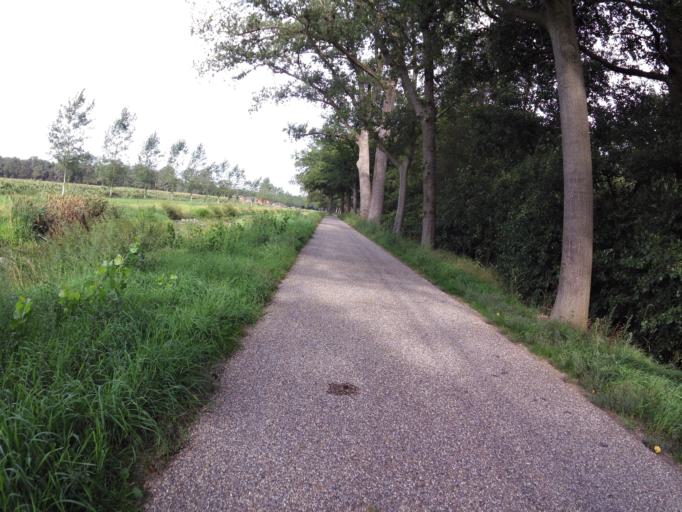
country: NL
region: Gelderland
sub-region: Oude IJsselstreek
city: Varsseveld
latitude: 51.9587
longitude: 6.4517
